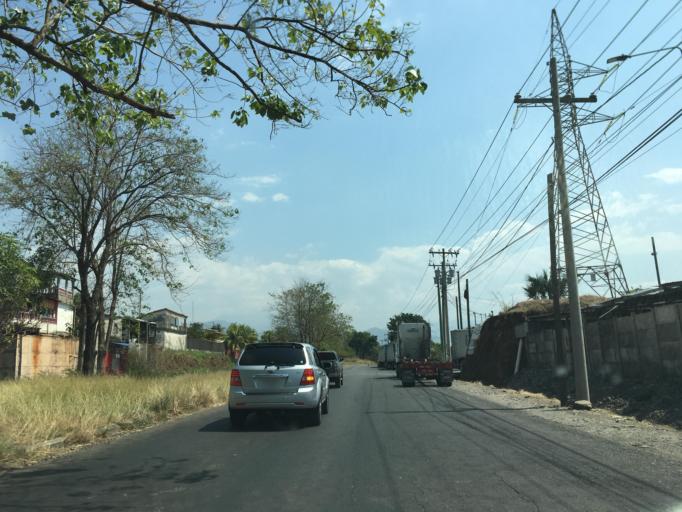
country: GT
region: Escuintla
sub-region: Municipio de Escuintla
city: Escuintla
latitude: 14.2766
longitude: -90.7667
